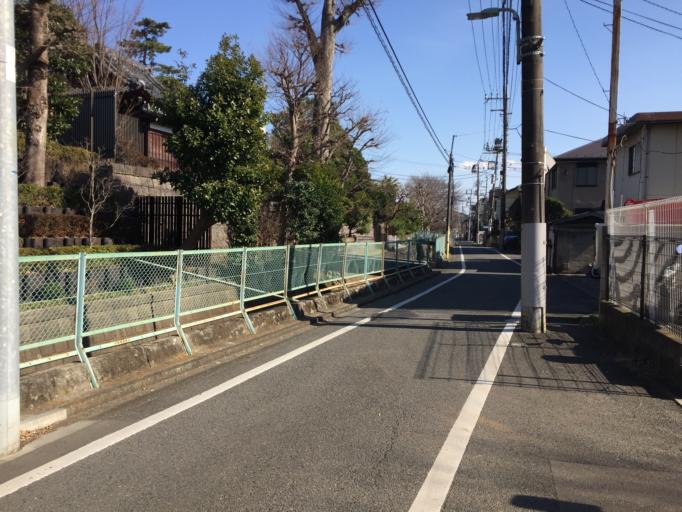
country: JP
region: Kanagawa
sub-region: Kawasaki-shi
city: Kawasaki
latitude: 35.5945
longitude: 139.6576
